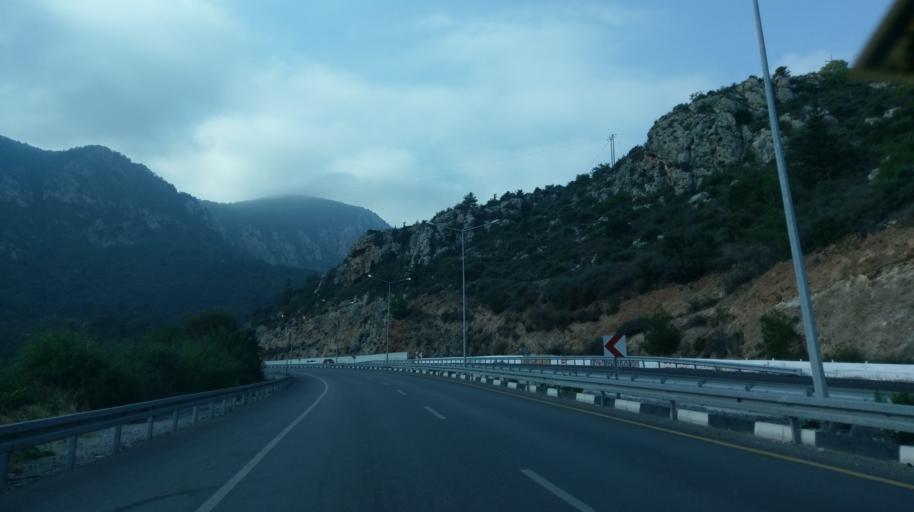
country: CY
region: Keryneia
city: Kyrenia
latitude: 35.3098
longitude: 33.3233
